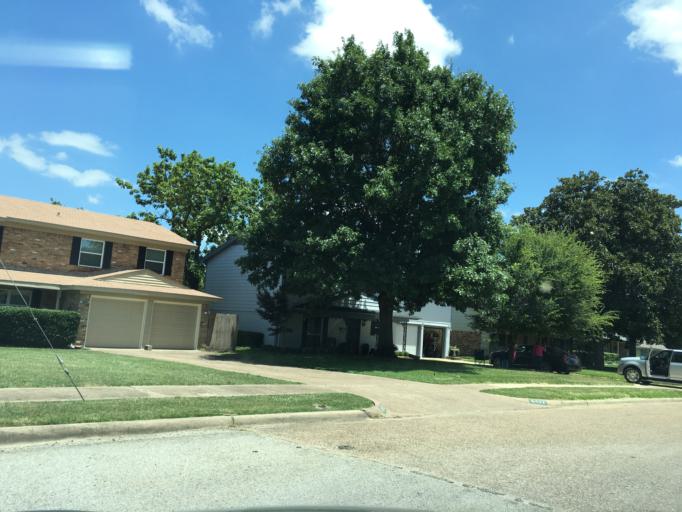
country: US
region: Texas
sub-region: Dallas County
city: Garland
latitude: 32.8354
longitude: -96.6486
